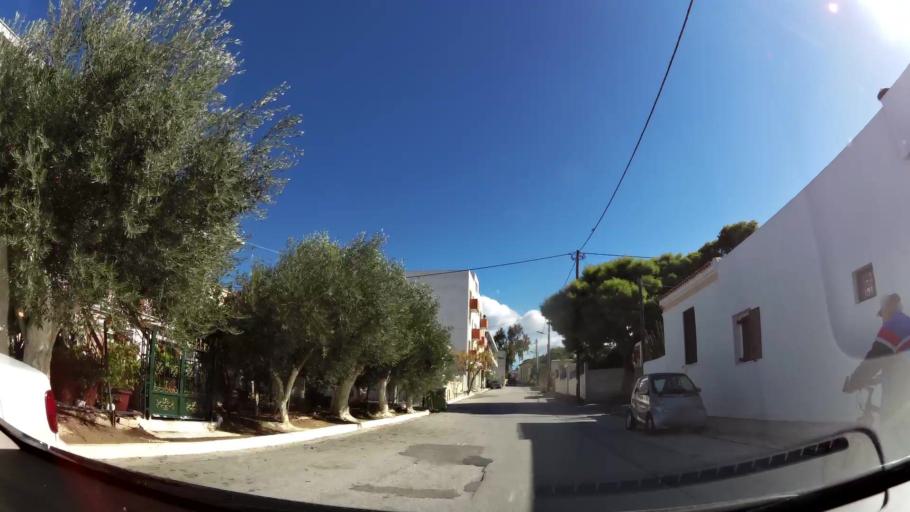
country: GR
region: Attica
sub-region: Nomarchia Anatolikis Attikis
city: Markopoulo
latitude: 37.8863
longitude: 23.9329
